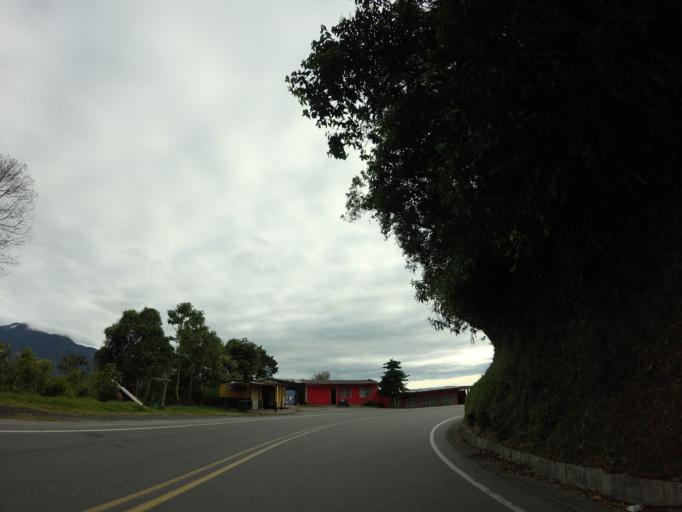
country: CO
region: Tolima
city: Herveo
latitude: 5.1122
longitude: -75.2171
